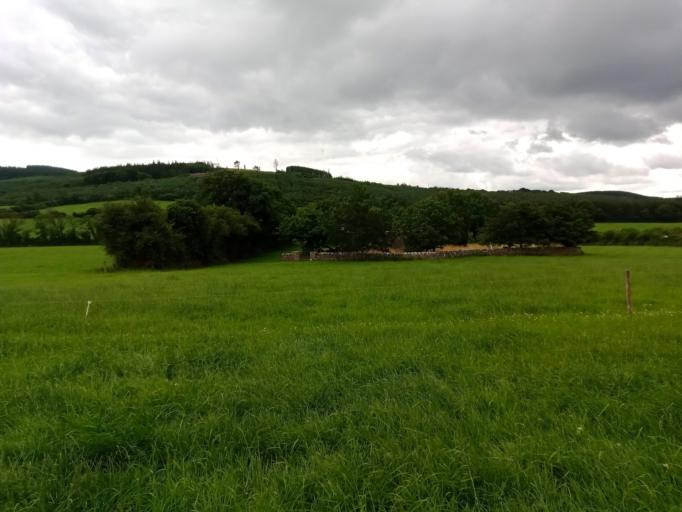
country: IE
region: Leinster
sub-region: Laois
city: Stradbally
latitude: 52.9583
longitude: -7.1902
